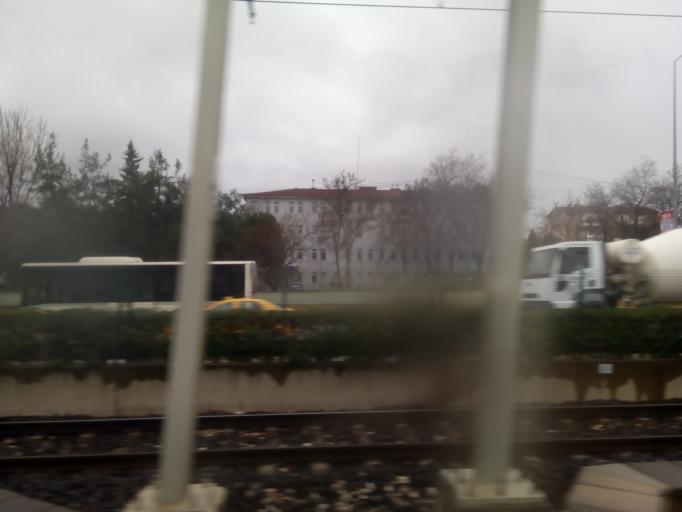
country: TR
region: Bursa
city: Niluefer
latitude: 40.2441
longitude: 28.9663
